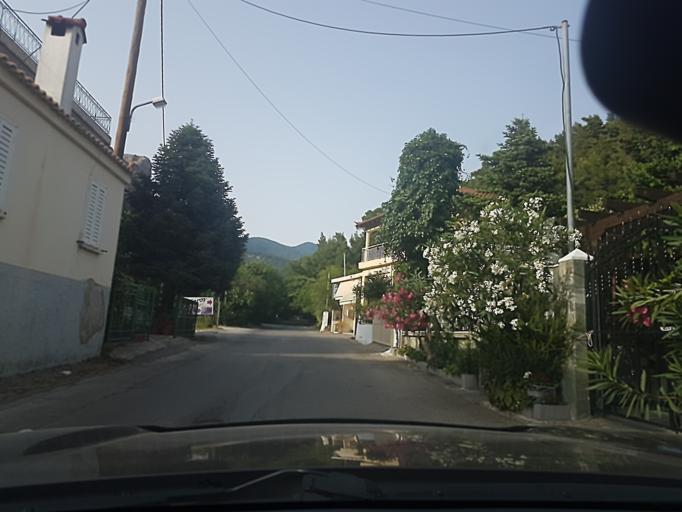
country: GR
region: Central Greece
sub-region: Nomos Evvoias
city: Yimnon
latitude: 38.5738
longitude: 23.8298
